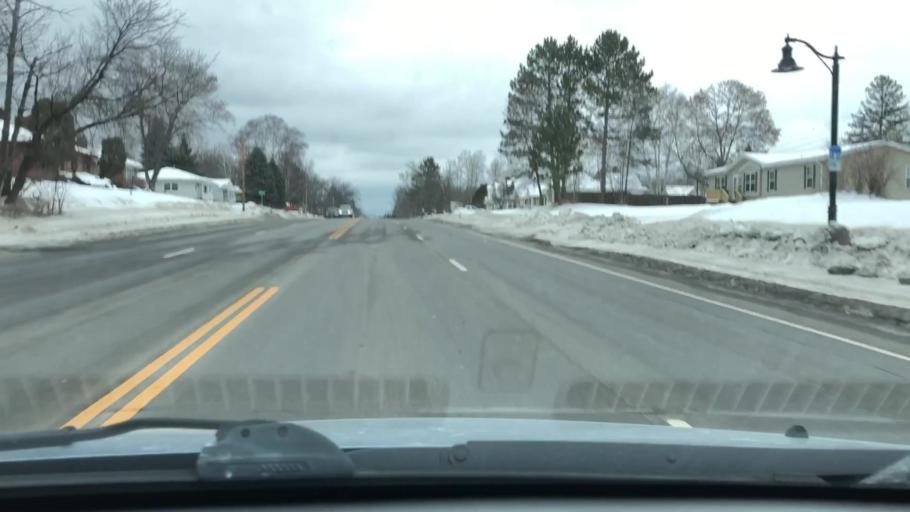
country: US
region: Minnesota
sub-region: Saint Louis County
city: Proctor
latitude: 46.7176
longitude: -92.1994
